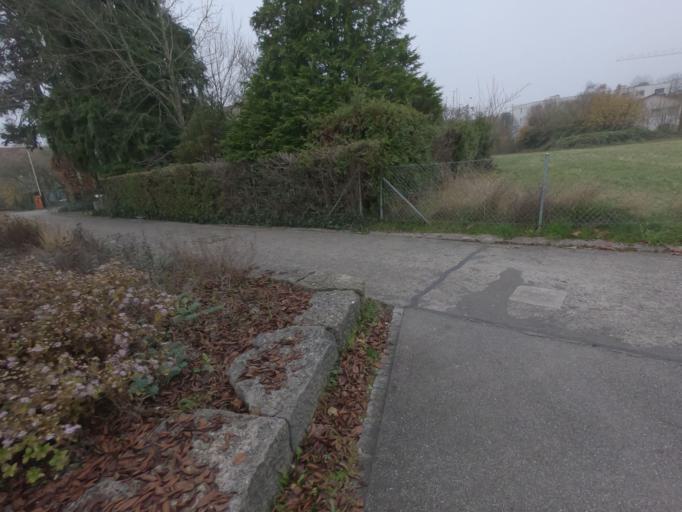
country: CH
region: Solothurn
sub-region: Bezirk Lebern
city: Grenchen
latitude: 47.1915
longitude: 7.3989
